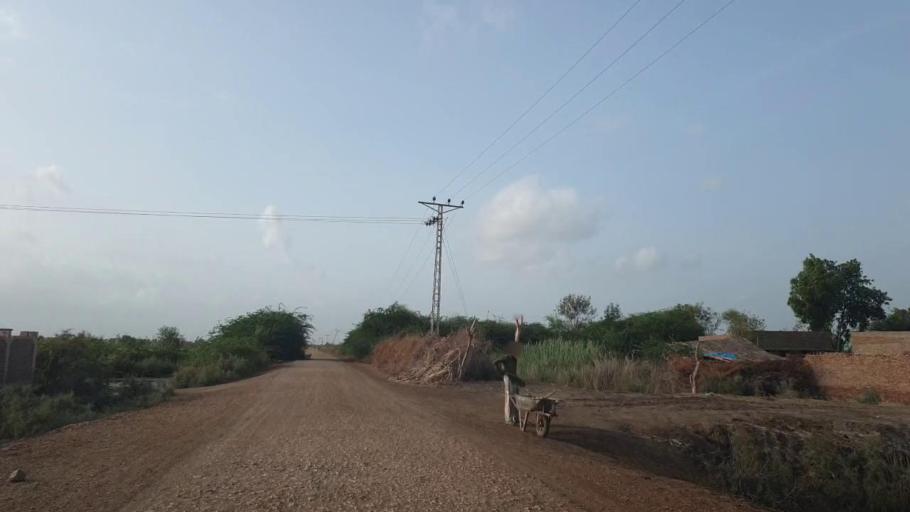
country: PK
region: Sindh
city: Tando Bago
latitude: 24.6472
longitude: 69.1118
